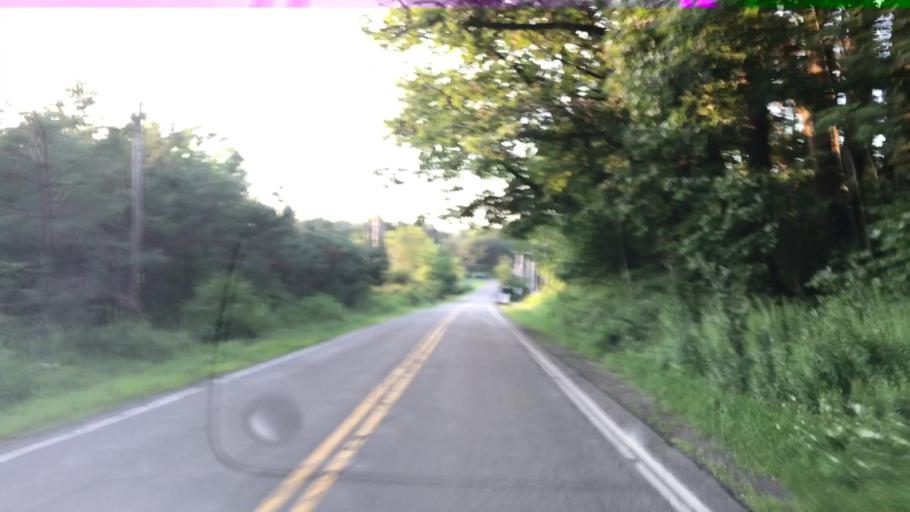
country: US
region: New York
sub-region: Chautauqua County
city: Mayville
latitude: 42.2607
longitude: -79.4697
